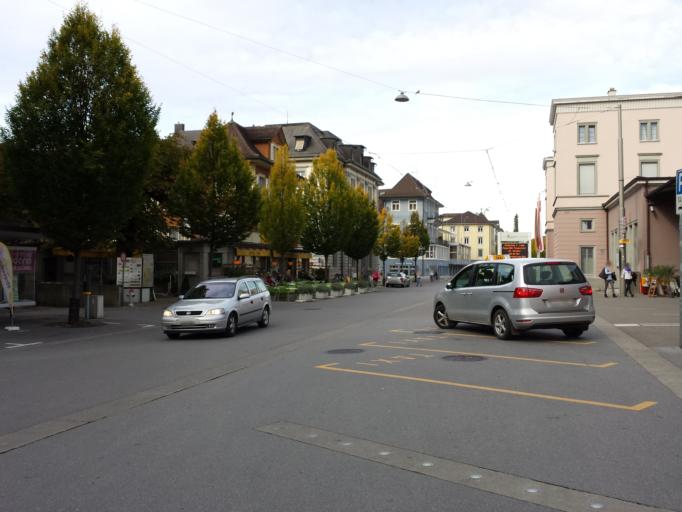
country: CH
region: Thurgau
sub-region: Arbon District
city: Romanshorn
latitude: 47.5649
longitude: 9.3791
